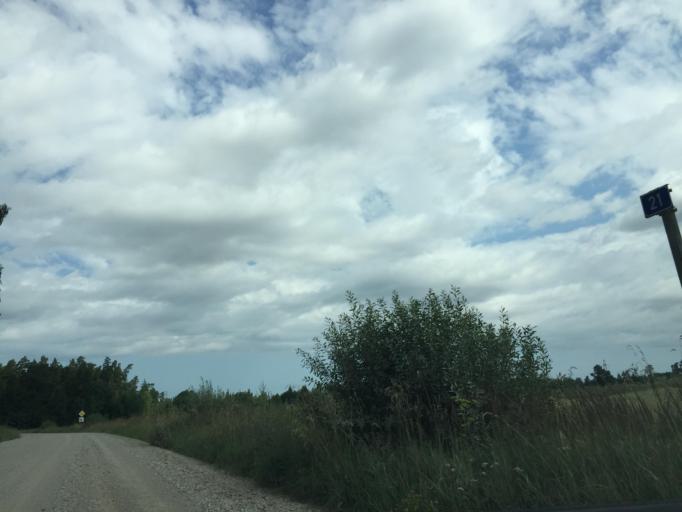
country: LV
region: Kandava
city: Kandava
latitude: 57.0279
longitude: 22.8185
